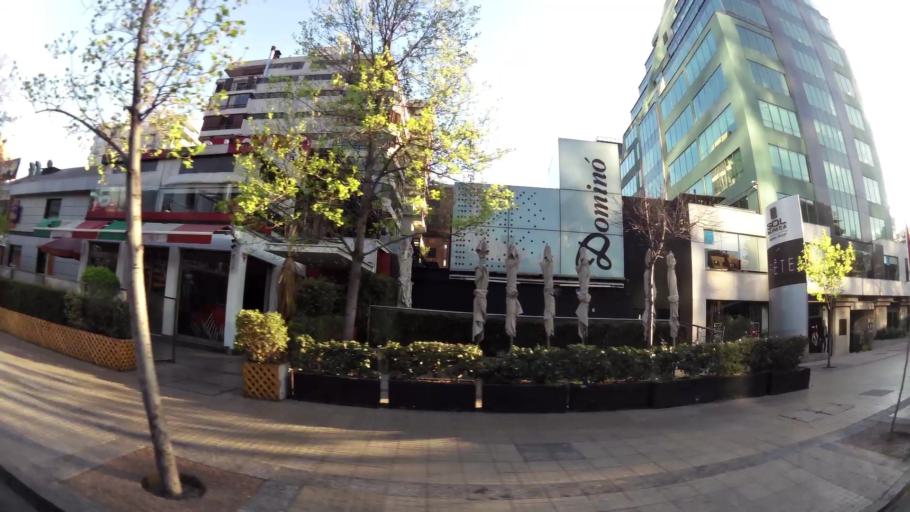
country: CL
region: Santiago Metropolitan
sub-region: Provincia de Santiago
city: Villa Presidente Frei, Nunoa, Santiago, Chile
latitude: -33.4140
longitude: -70.6008
